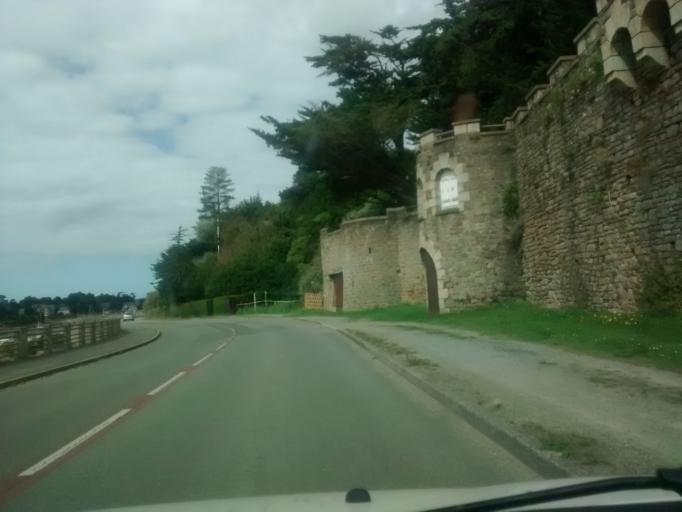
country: FR
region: Brittany
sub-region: Departement d'Ille-et-Vilaine
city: Saint-Briac-sur-Mer
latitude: 48.6190
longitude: -2.1371
